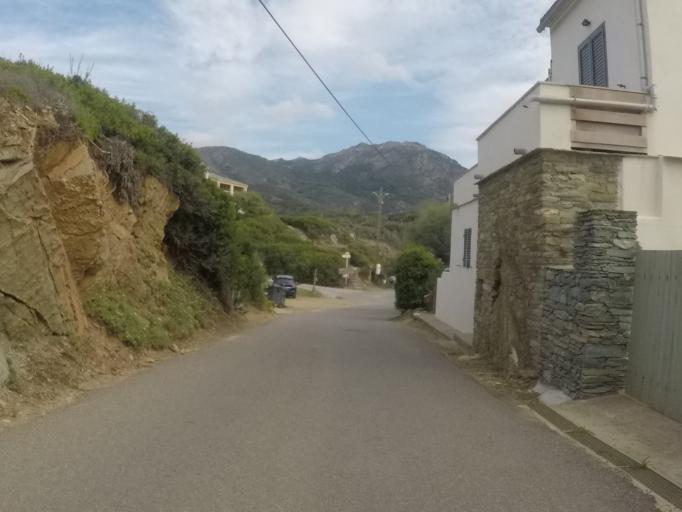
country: FR
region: Corsica
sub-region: Departement de la Haute-Corse
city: Brando
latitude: 42.9616
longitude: 9.3505
